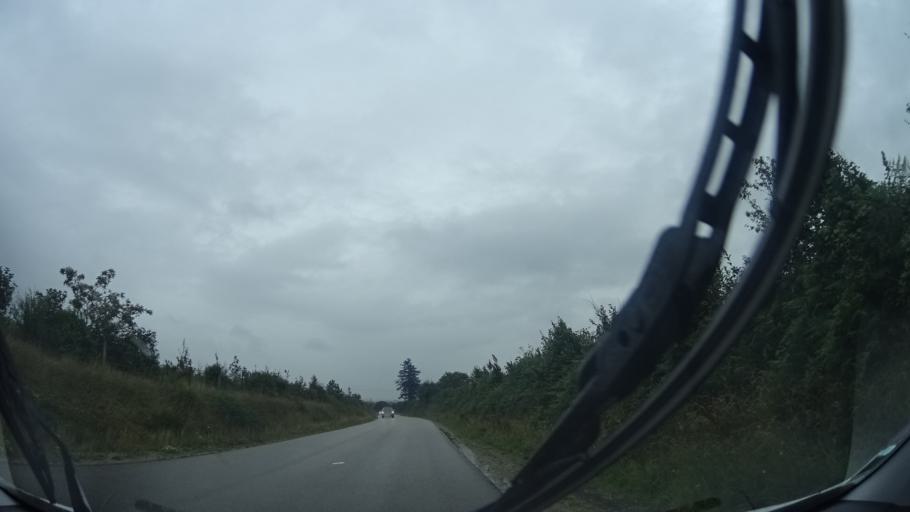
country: FR
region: Lower Normandy
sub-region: Departement de la Manche
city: Urville-Nacqueville
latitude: 49.5956
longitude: -1.7643
